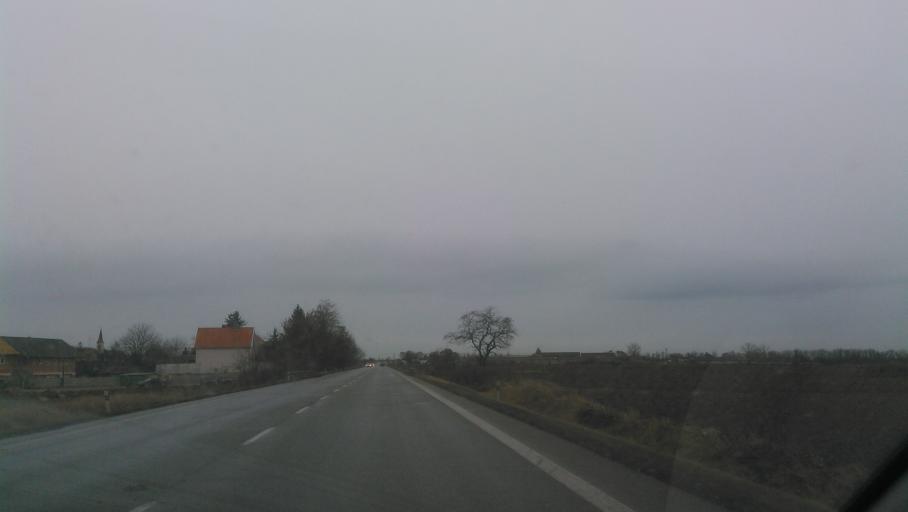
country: SK
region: Nitriansky
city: Sellye
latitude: 48.1681
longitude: 17.8354
